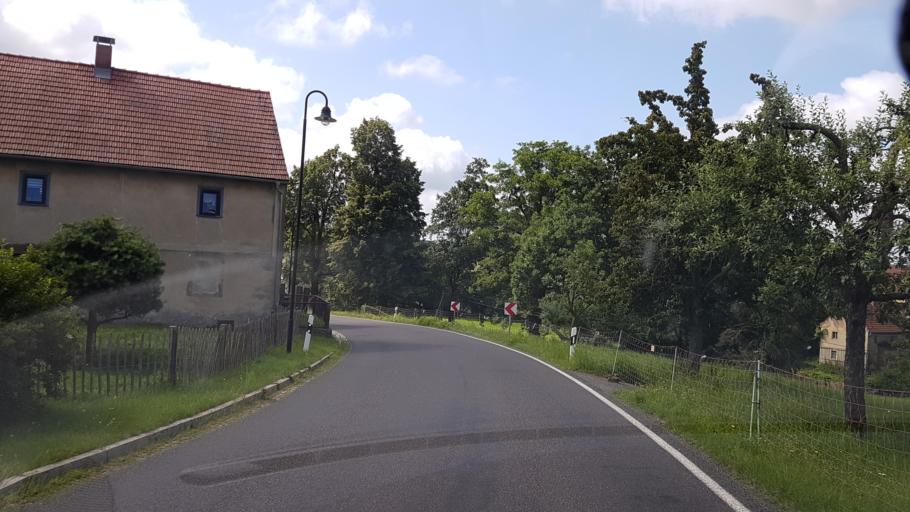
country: DE
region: Saxony
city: Wachau
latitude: 51.1665
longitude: 13.9068
